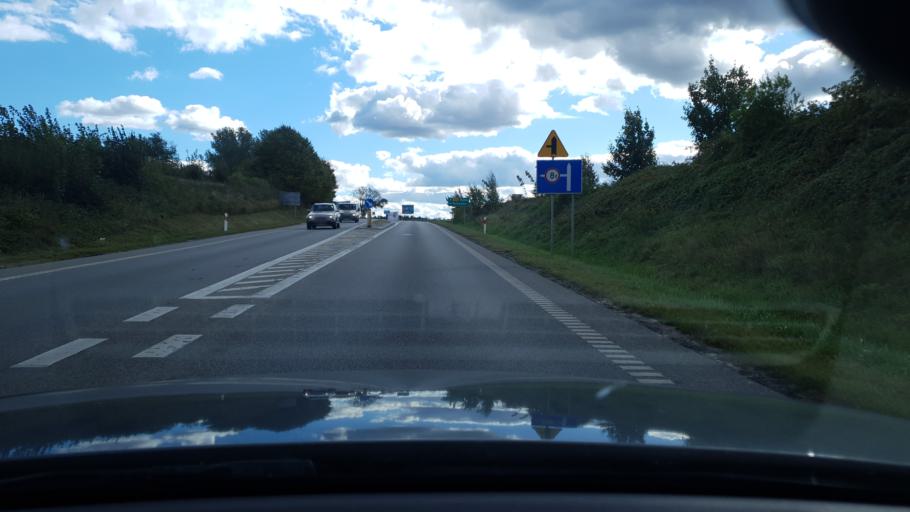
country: PL
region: Pomeranian Voivodeship
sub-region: Powiat wejherowski
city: Rekowo Dolne
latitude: 54.6571
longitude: 18.3624
